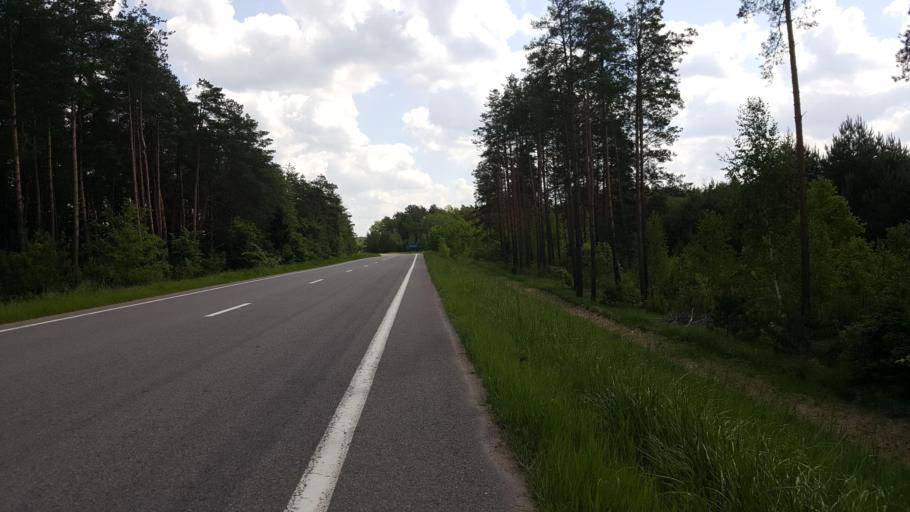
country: BY
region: Brest
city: Zhabinka
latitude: 52.3978
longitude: 24.0595
